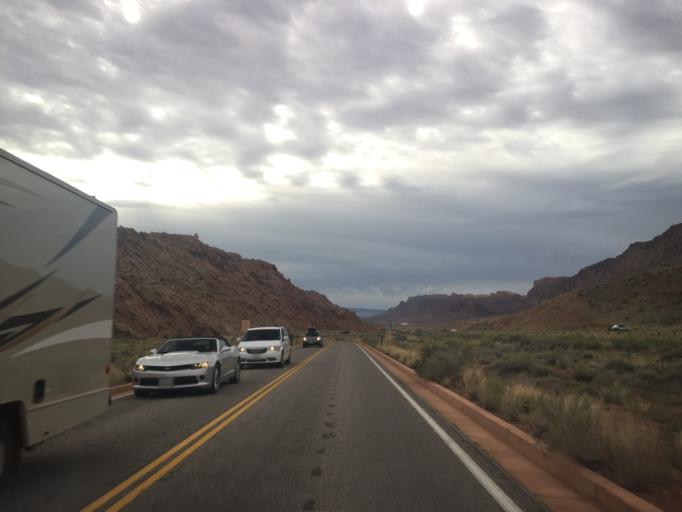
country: US
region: Utah
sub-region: Grand County
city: Moab
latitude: 38.6130
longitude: -109.6099
